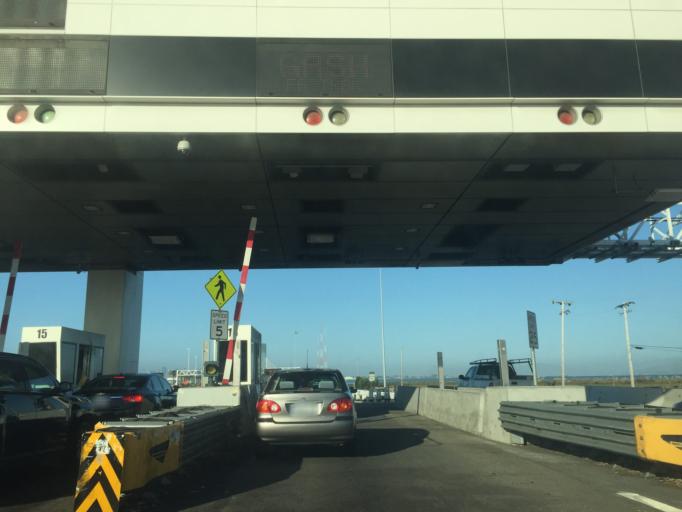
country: US
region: California
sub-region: Alameda County
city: Emeryville
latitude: 37.8251
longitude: -122.3137
